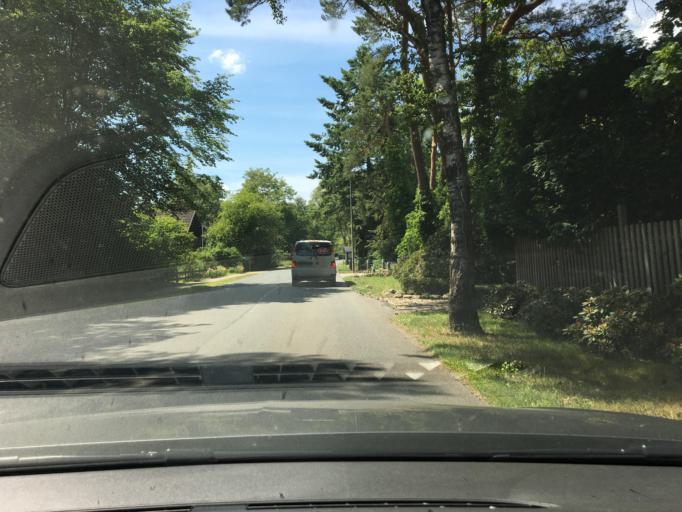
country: DE
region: Lower Saxony
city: Worpswede
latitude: 53.2567
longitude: 8.9785
